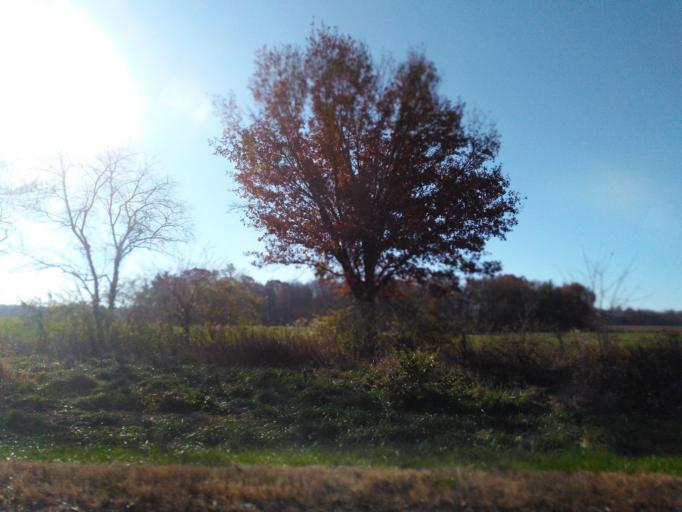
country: US
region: Illinois
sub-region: Madison County
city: Saint Jacob
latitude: 38.7648
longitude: -89.7719
